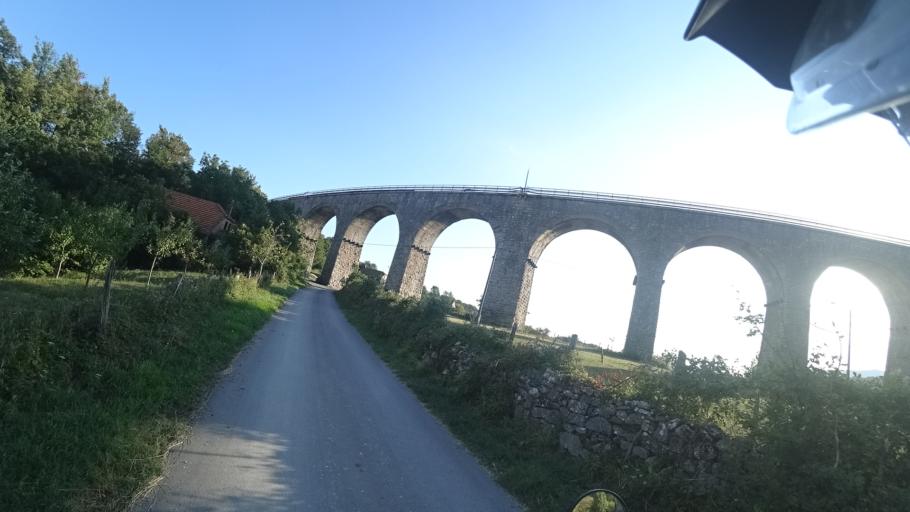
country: HR
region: Sibensko-Kniniska
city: Knin
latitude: 44.1349
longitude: 16.1337
